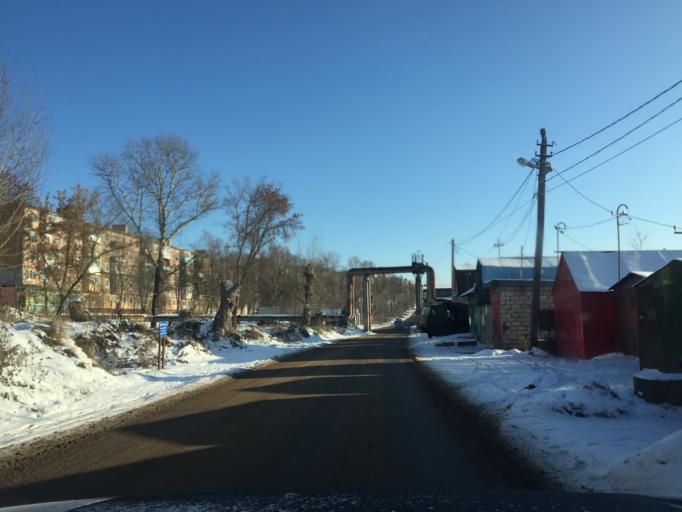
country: RU
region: Tula
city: Tula
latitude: 54.1914
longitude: 37.6777
